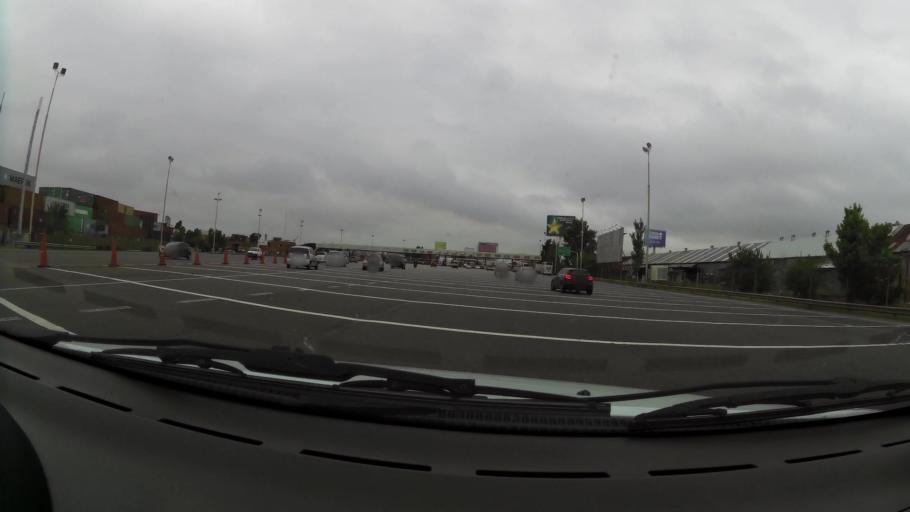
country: AR
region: Buenos Aires F.D.
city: Retiro
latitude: -34.5744
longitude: -58.3953
